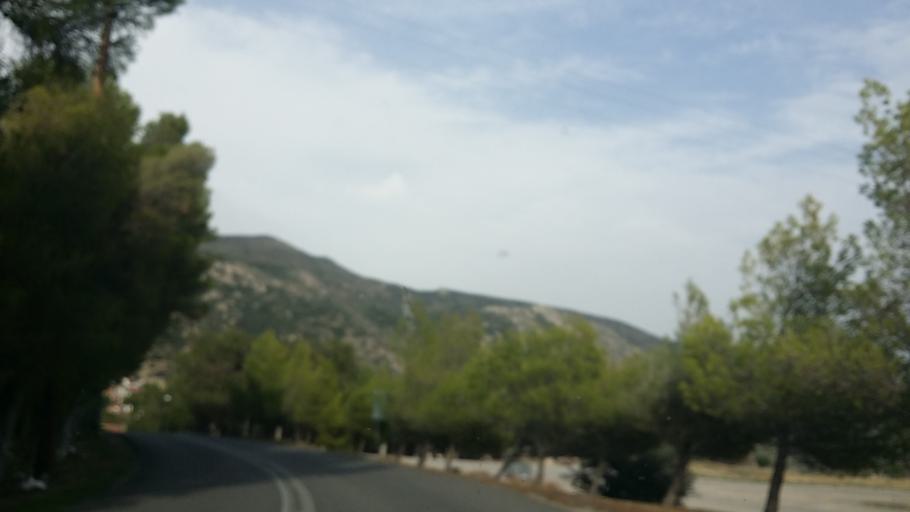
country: GR
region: Central Greece
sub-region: Nomos Voiotias
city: Korini
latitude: 38.2560
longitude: 22.9068
